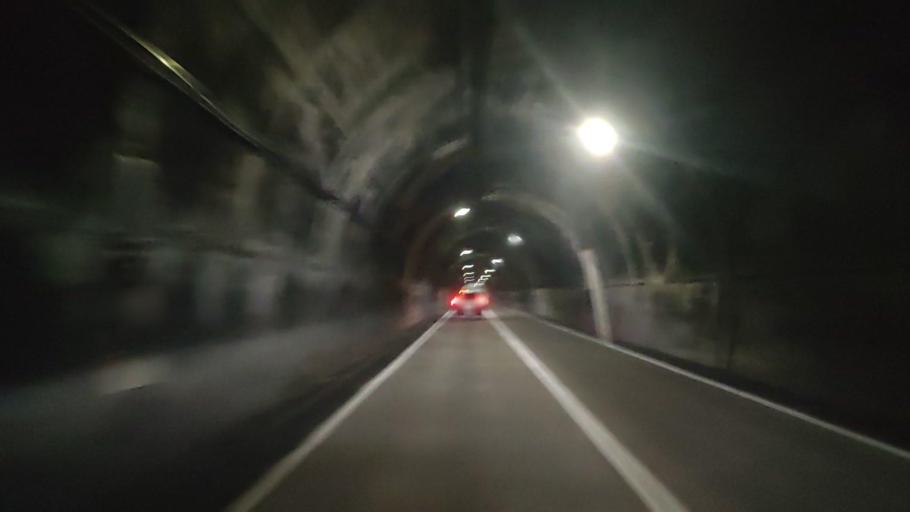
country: JP
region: Mie
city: Ise
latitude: 34.4132
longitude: 136.7636
